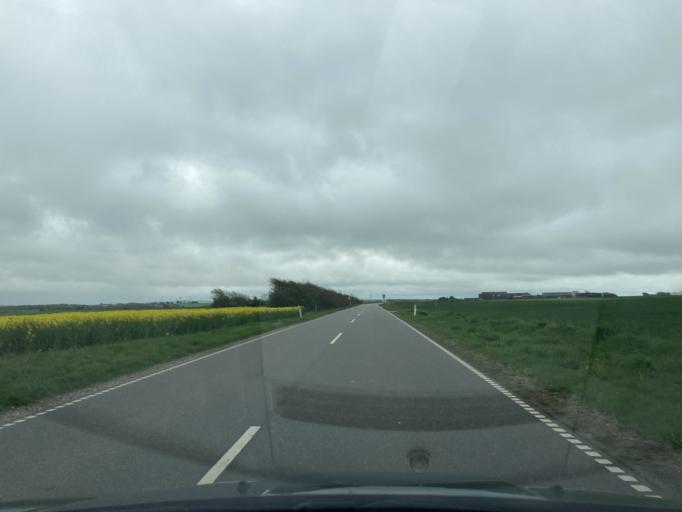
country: DK
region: North Denmark
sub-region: Thisted Kommune
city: Hurup
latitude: 56.8325
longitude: 8.3600
